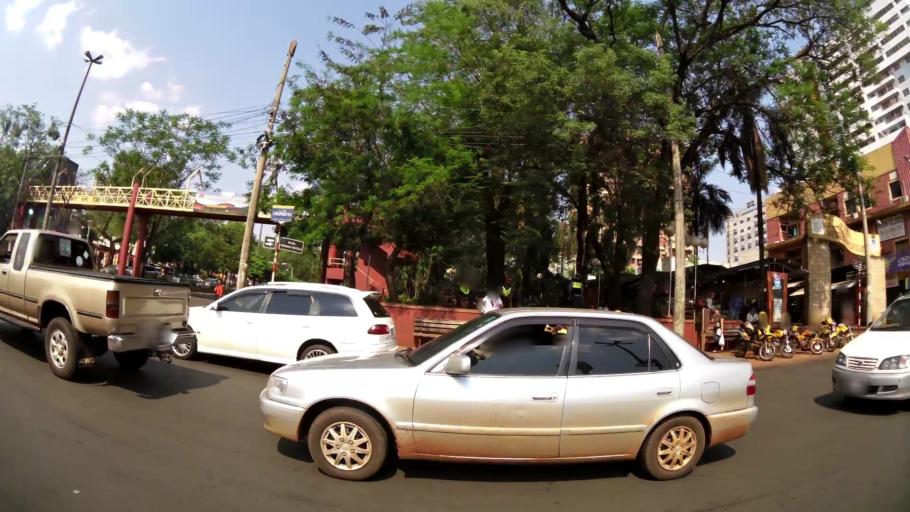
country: PY
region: Alto Parana
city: Ciudad del Este
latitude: -25.5096
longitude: -54.6152
